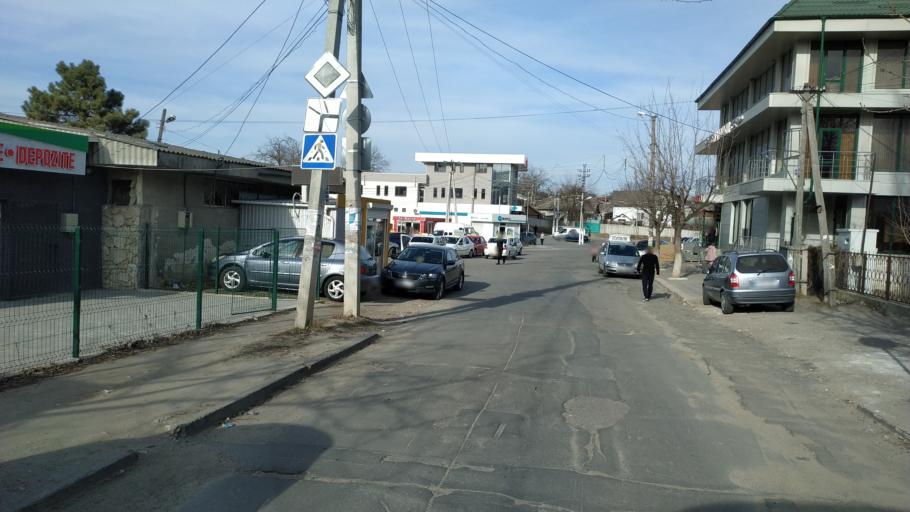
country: MD
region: Chisinau
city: Vatra
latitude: 47.0716
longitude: 28.6843
